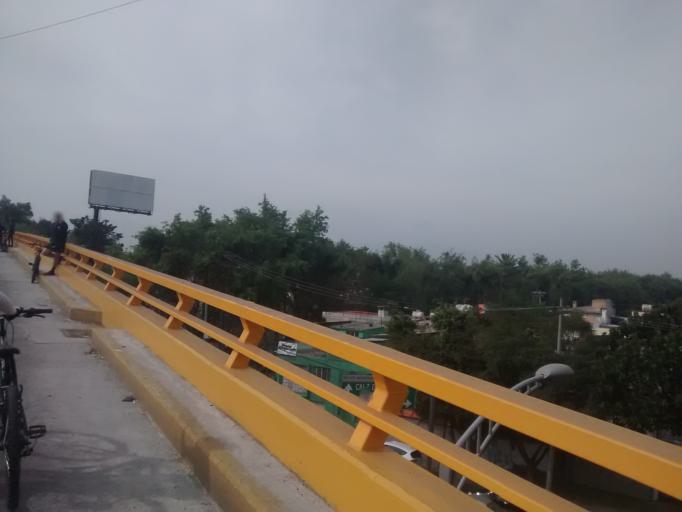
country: MX
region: Mexico City
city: Colonia Nativitas
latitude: 19.3612
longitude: -99.1298
